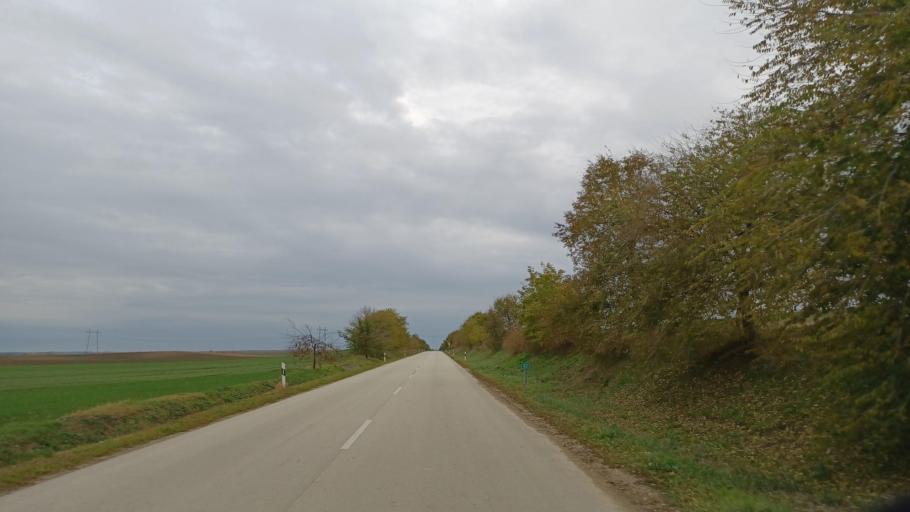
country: HU
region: Tolna
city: Nagydorog
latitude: 46.6759
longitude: 18.6008
